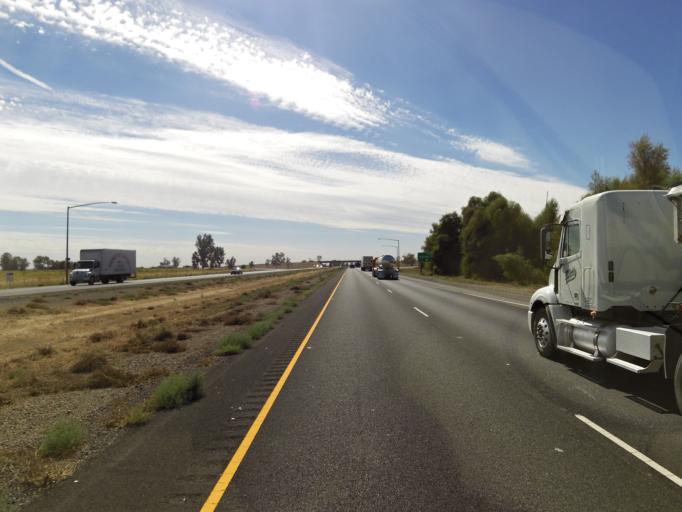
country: US
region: California
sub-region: Colusa County
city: Maxwell
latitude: 39.2815
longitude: -122.1834
